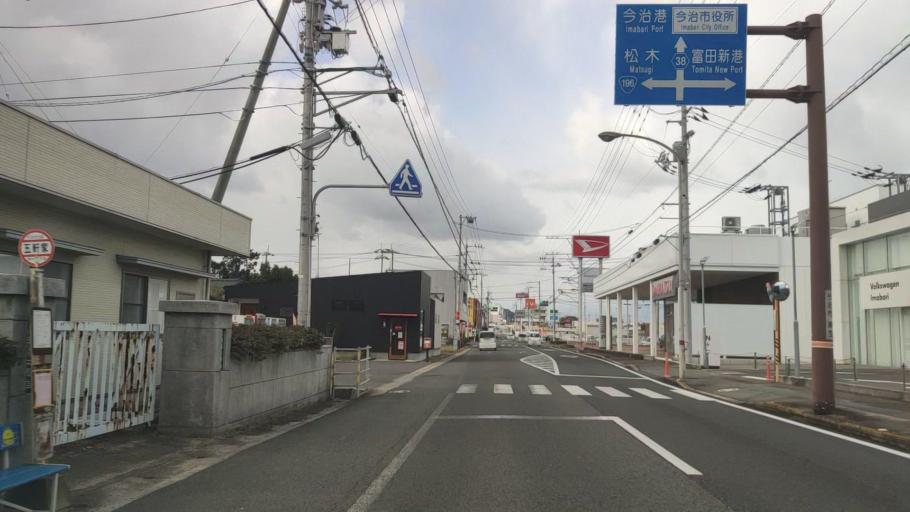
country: JP
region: Ehime
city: Saijo
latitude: 34.0459
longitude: 133.0203
